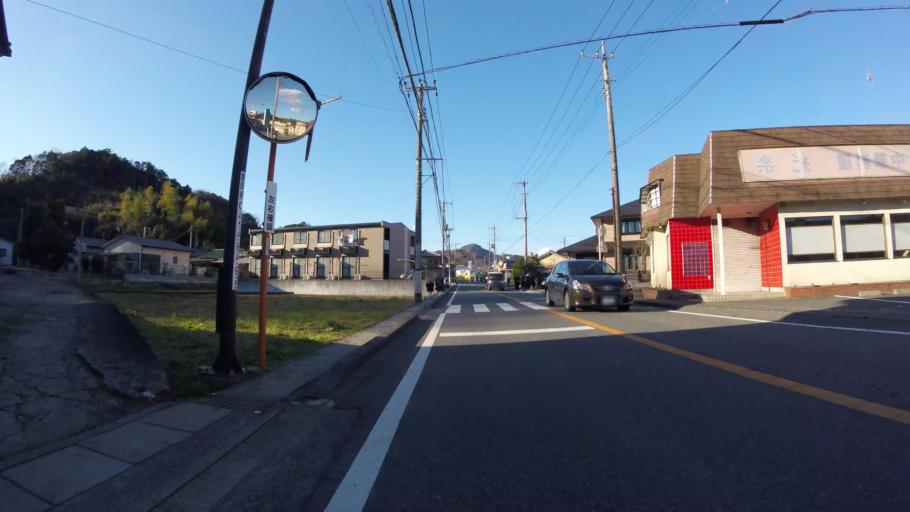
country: JP
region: Shizuoka
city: Mishima
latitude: 35.0355
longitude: 138.9280
